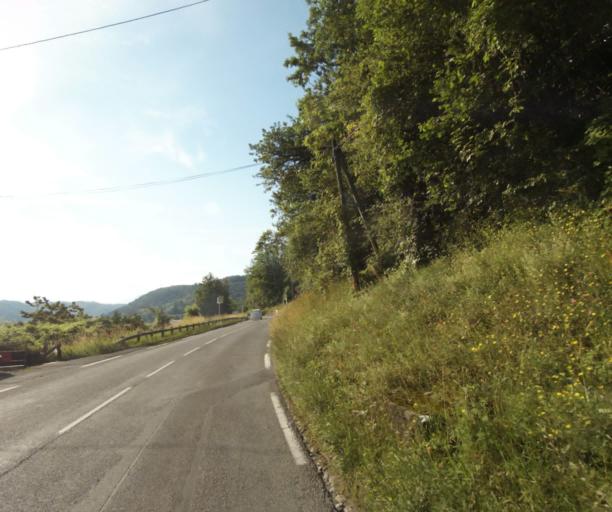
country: FR
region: Rhone-Alpes
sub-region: Departement de la Haute-Savoie
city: Thonon-les-Bains
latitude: 46.3689
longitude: 6.4936
